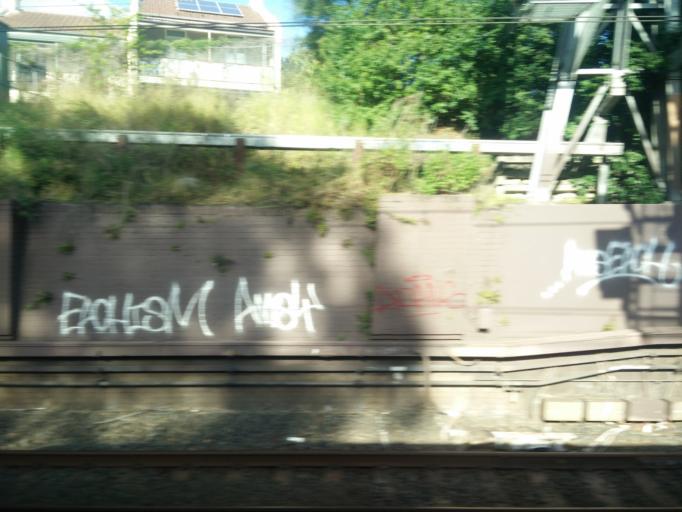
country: AU
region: New South Wales
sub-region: Marrickville
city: Lewisham
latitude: -33.8940
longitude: 151.1583
